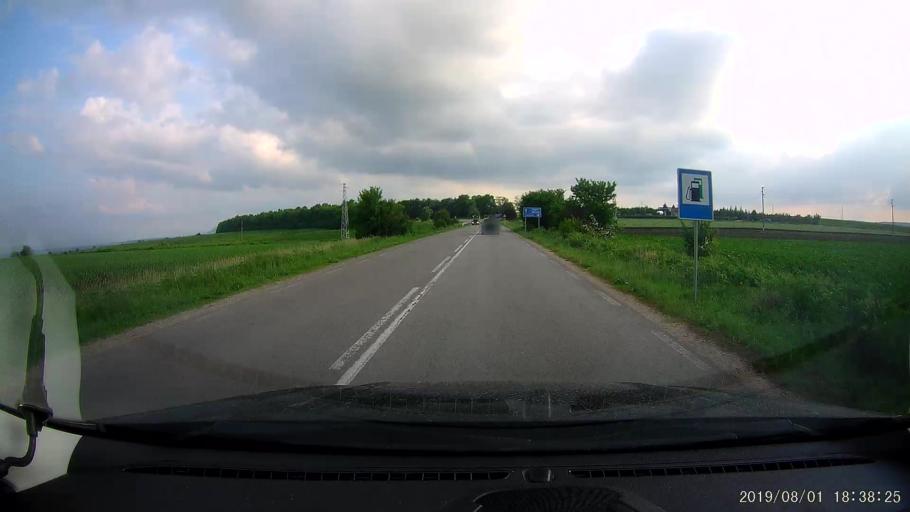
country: BG
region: Shumen
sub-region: Obshtina Khitrino
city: Gara Khitrino
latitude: 43.4024
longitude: 26.9171
